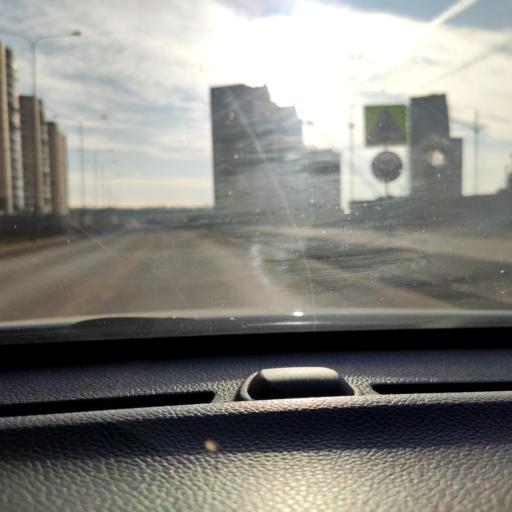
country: RU
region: Voronezj
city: Shilovo
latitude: 51.5691
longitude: 39.1217
